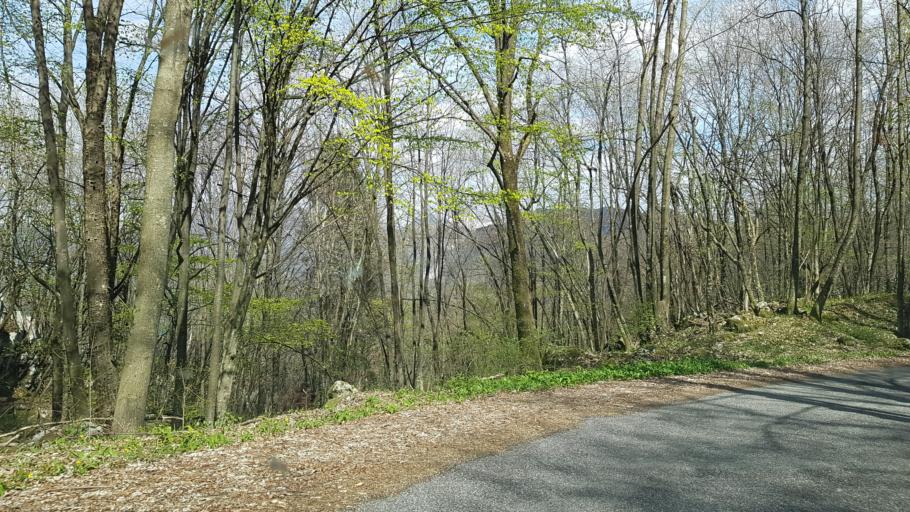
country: IT
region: Friuli Venezia Giulia
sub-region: Provincia di Udine
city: Trasaghis
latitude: 46.2867
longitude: 13.0299
